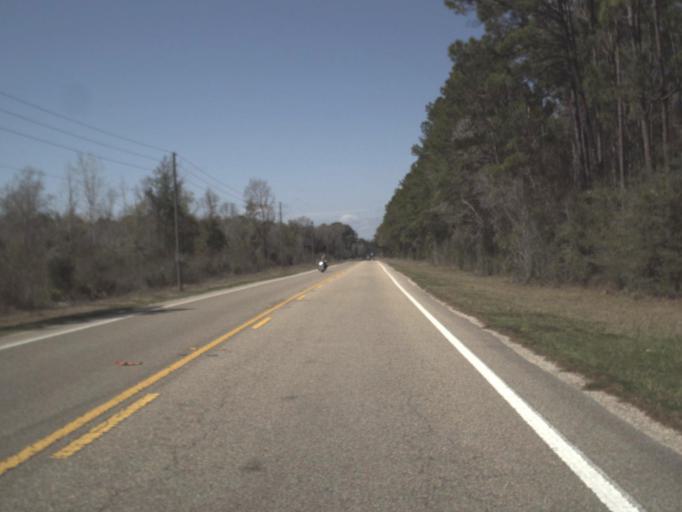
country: US
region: Florida
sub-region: Leon County
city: Woodville
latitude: 30.2267
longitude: -84.2151
